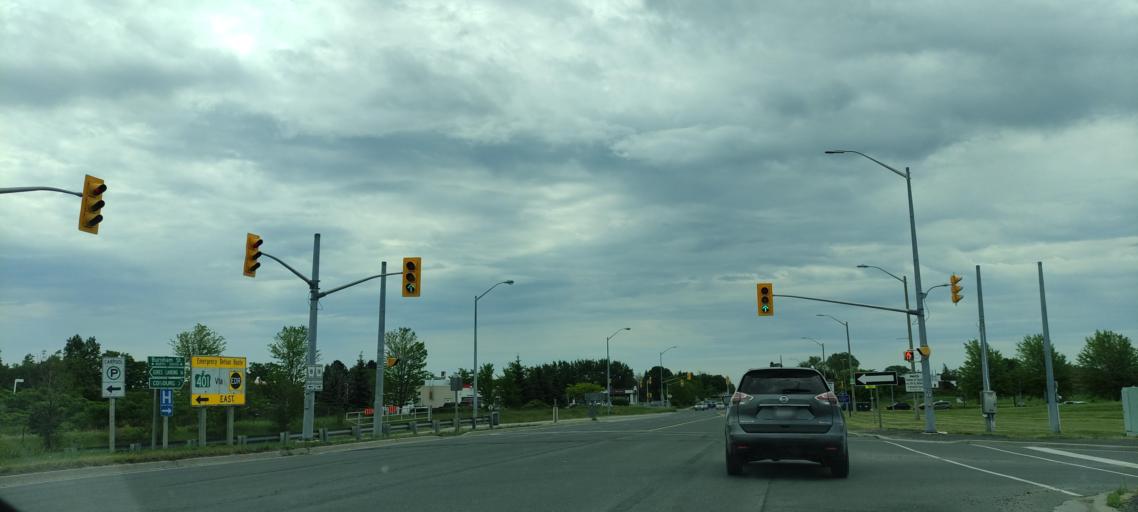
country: CA
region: Ontario
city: Cobourg
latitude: 43.9789
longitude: -78.1958
